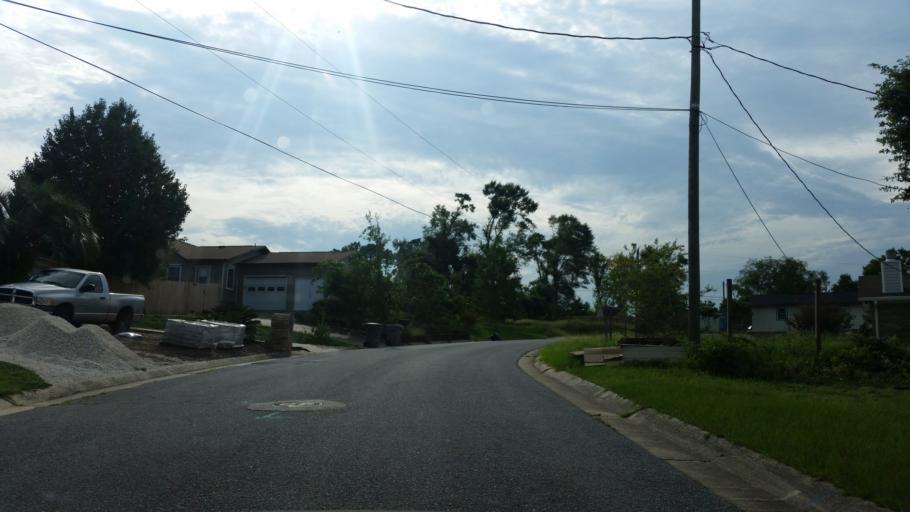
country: US
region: Florida
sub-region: Escambia County
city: Ferry Pass
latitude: 30.5112
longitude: -87.1739
